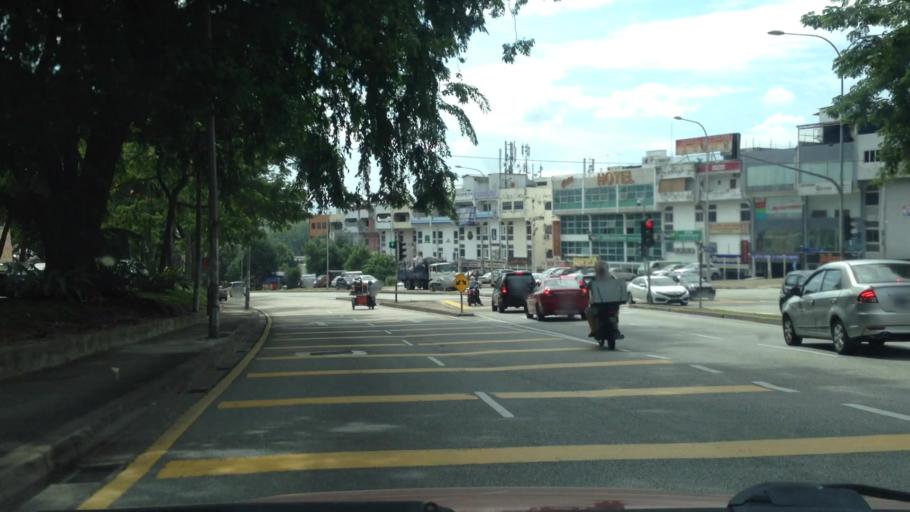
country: MY
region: Kuala Lumpur
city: Kuala Lumpur
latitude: 3.0908
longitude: 101.6805
